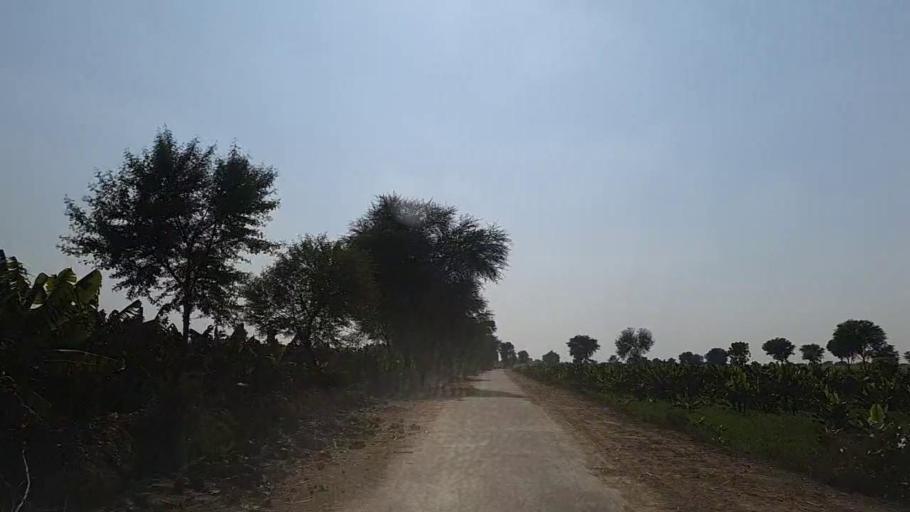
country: PK
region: Sindh
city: Daur
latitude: 26.4870
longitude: 68.2507
